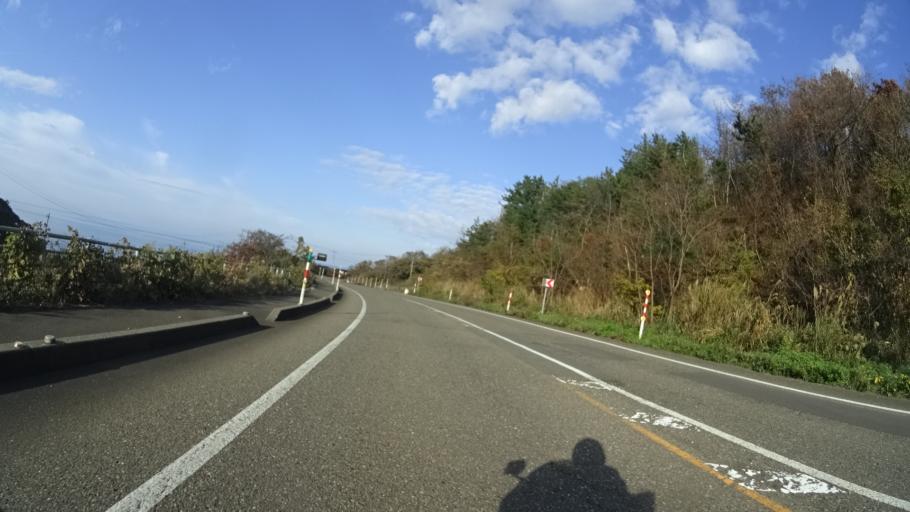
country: JP
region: Niigata
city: Kashiwazaki
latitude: 37.3374
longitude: 138.4736
